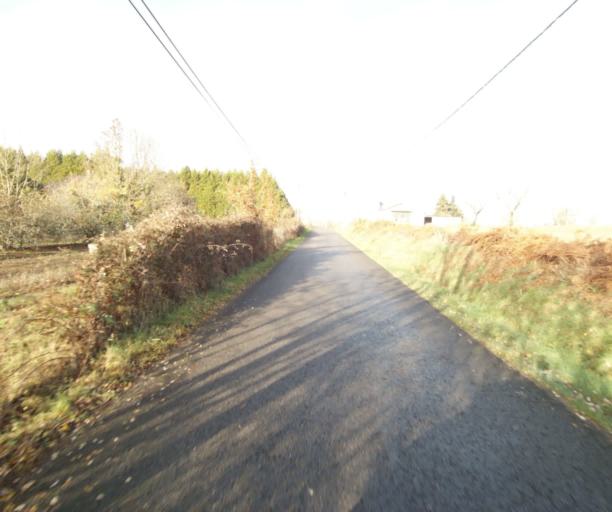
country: FR
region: Limousin
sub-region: Departement de la Correze
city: Cornil
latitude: 45.2086
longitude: 1.7092
